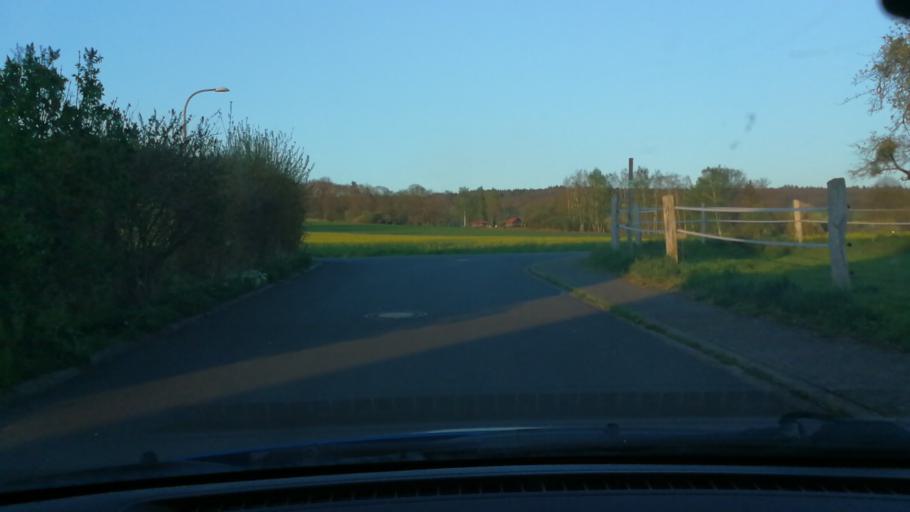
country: DE
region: Lower Saxony
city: Bodenfelde
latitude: 51.5938
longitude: 9.5942
